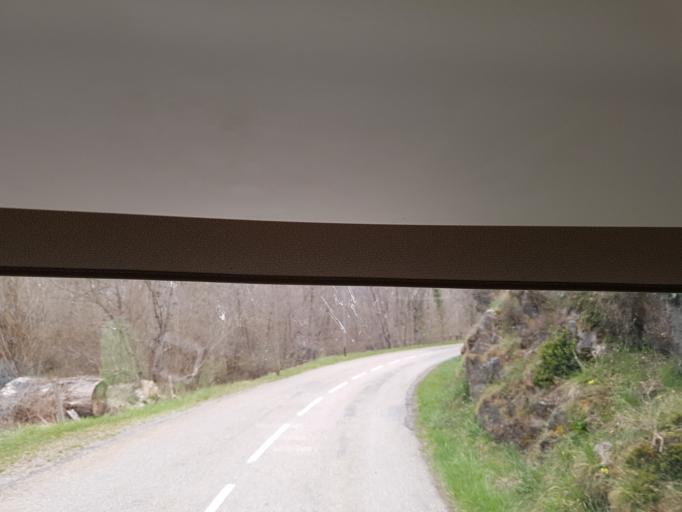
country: FR
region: Languedoc-Roussillon
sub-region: Departement de l'Aude
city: Quillan
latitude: 42.7385
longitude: 2.0874
